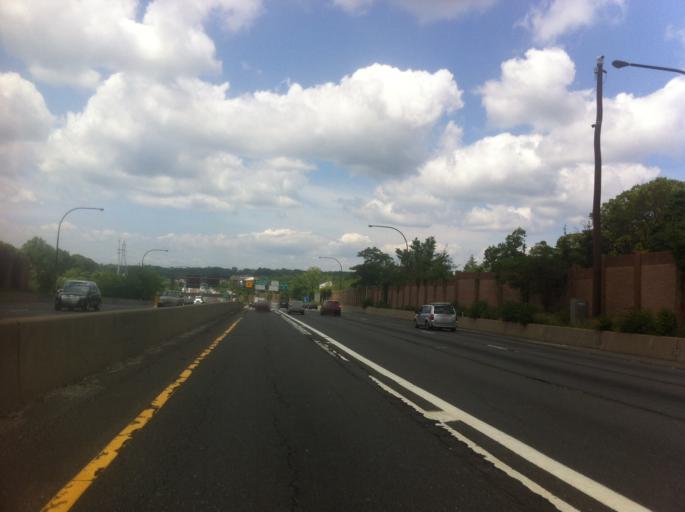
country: US
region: New York
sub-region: Nassau County
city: East Hills
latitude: 40.7846
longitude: -73.6350
